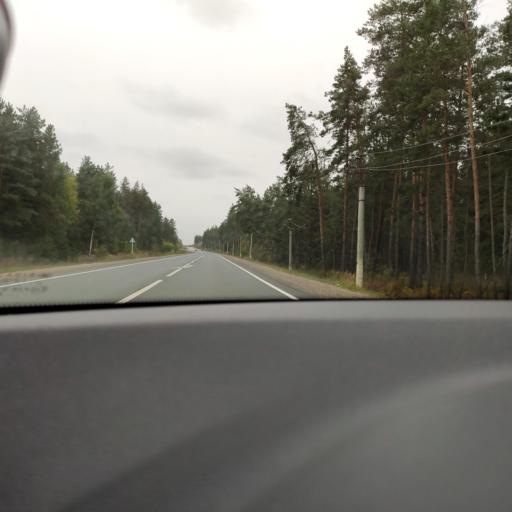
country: RU
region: Samara
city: Mirnyy
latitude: 53.5504
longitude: 50.2954
